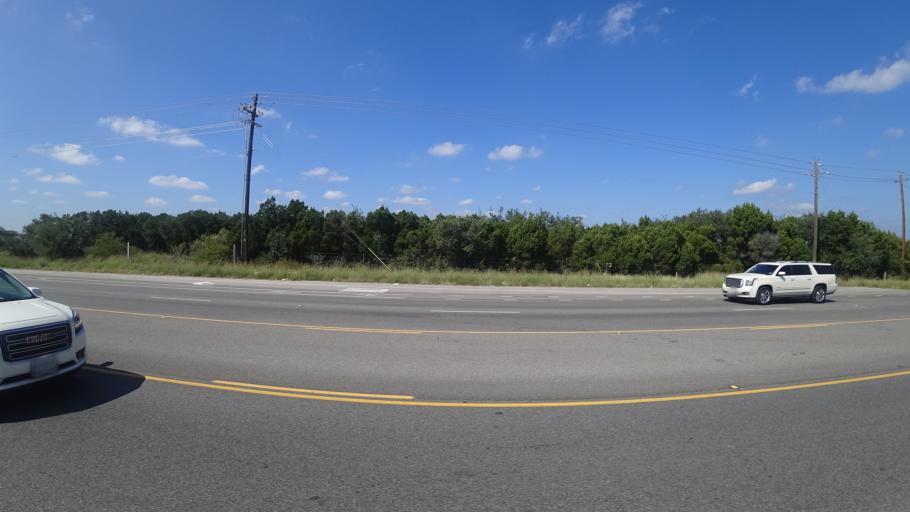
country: US
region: Texas
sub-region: Travis County
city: Lakeway
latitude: 30.3699
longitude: -97.9486
